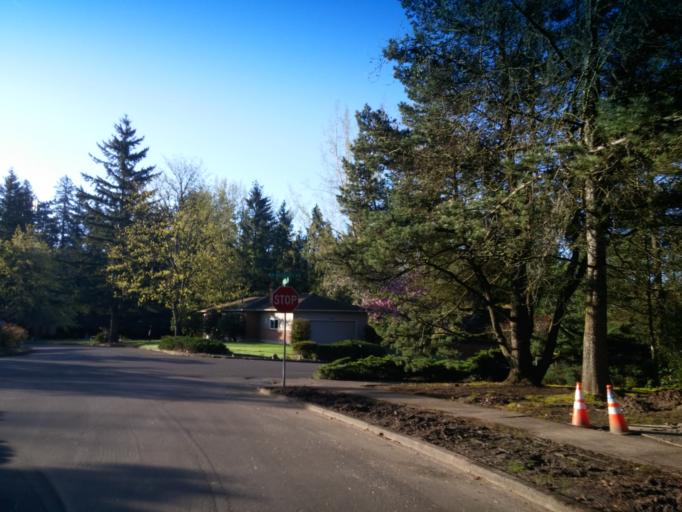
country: US
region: Oregon
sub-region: Washington County
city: Cedar Hills
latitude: 45.5021
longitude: -122.7903
